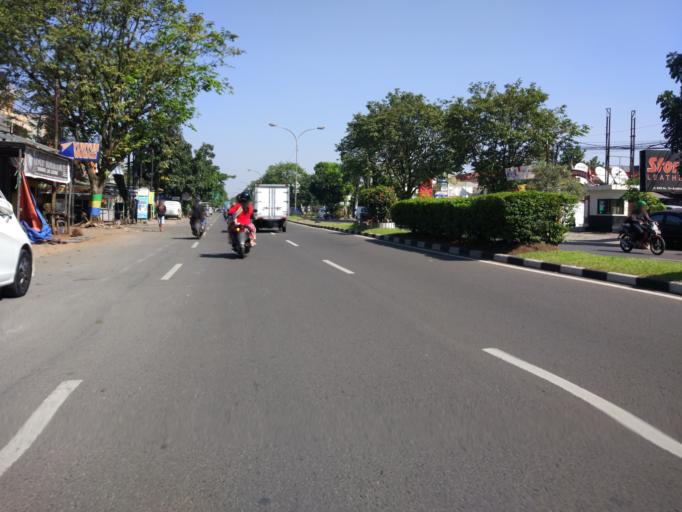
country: ID
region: West Java
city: Bandung
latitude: -6.9382
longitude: 107.6184
